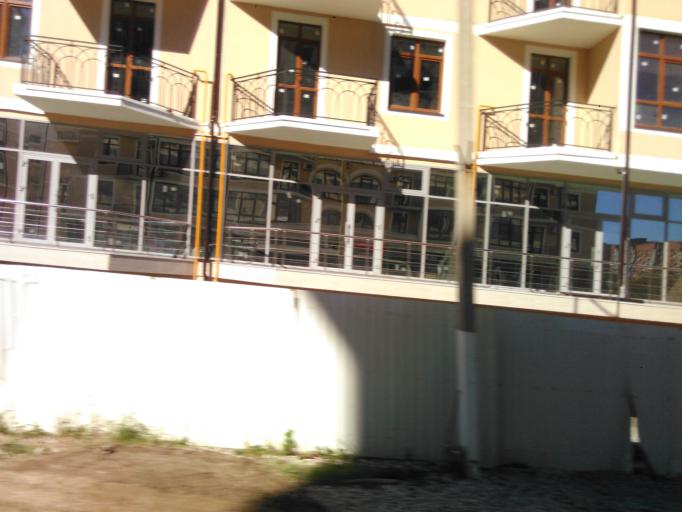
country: RU
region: Krasnodarskiy
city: Gelendzhik
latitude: 44.5499
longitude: 38.0610
